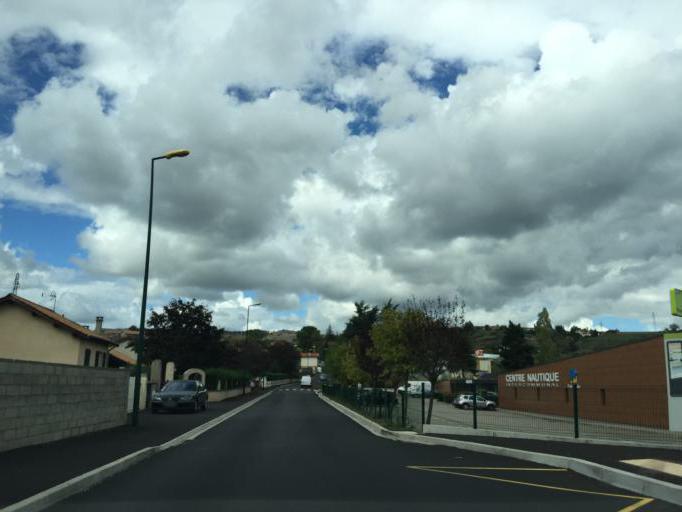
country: FR
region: Rhone-Alpes
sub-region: Departement de la Loire
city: Saint-Martin-la-Plaine
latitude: 45.5305
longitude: 4.5963
